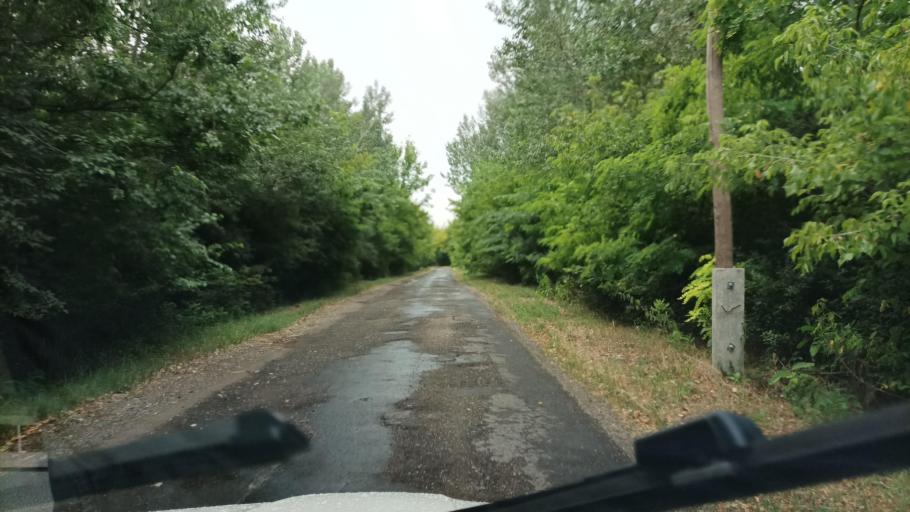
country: HU
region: Pest
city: Orkeny
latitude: 47.0419
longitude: 19.3506
